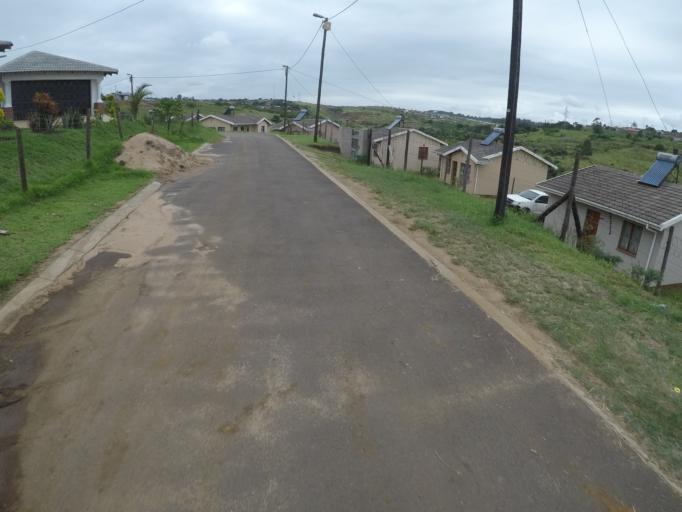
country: ZA
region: KwaZulu-Natal
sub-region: uThungulu District Municipality
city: Empangeni
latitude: -28.7707
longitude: 31.8733
